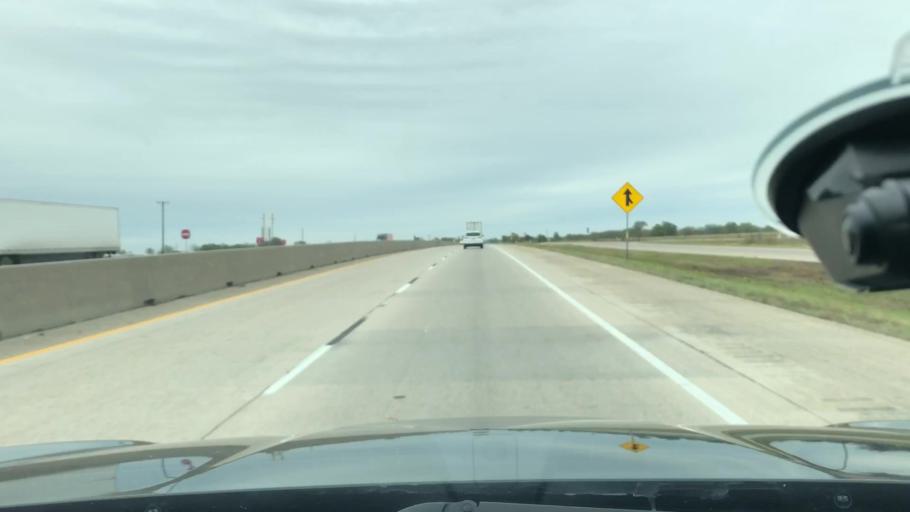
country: US
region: Texas
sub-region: Hunt County
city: Commerce
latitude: 33.1314
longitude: -95.8011
